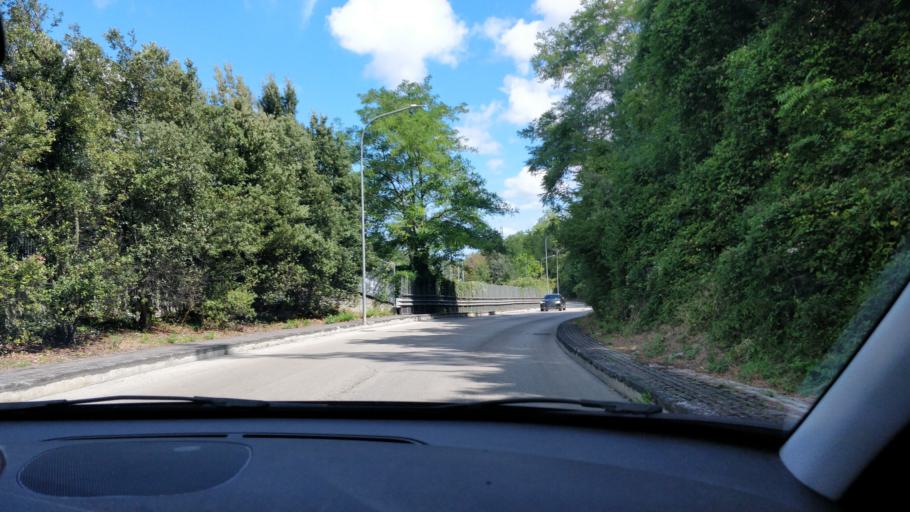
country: IT
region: Abruzzo
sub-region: Provincia di Chieti
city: Lanciano
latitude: 42.2285
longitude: 14.4028
